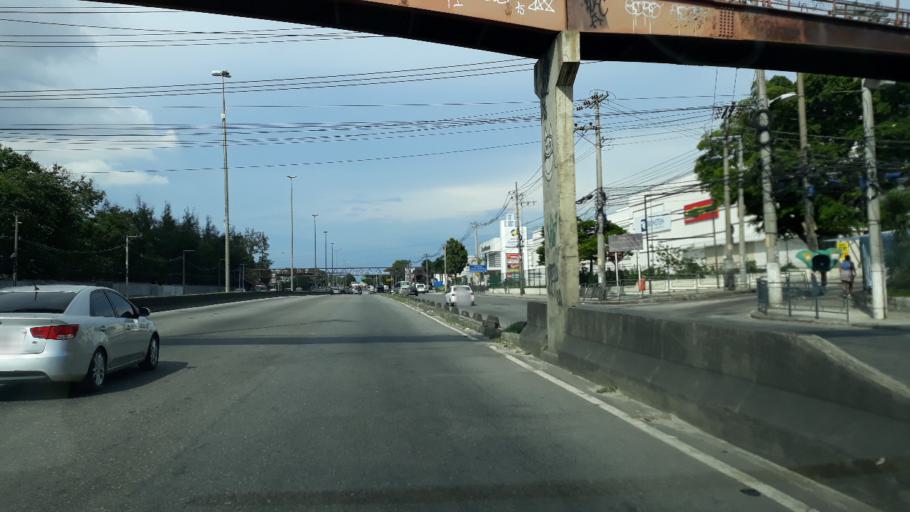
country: BR
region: Rio de Janeiro
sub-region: Sao Joao De Meriti
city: Sao Joao de Meriti
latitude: -22.8415
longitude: -43.3712
